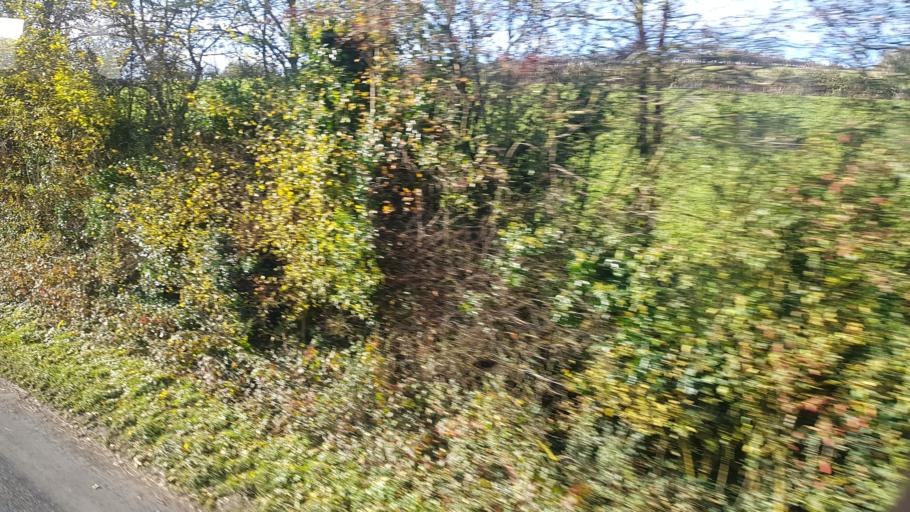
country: GB
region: England
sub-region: Isle of Wight
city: Newport
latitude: 50.6671
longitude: -1.3441
